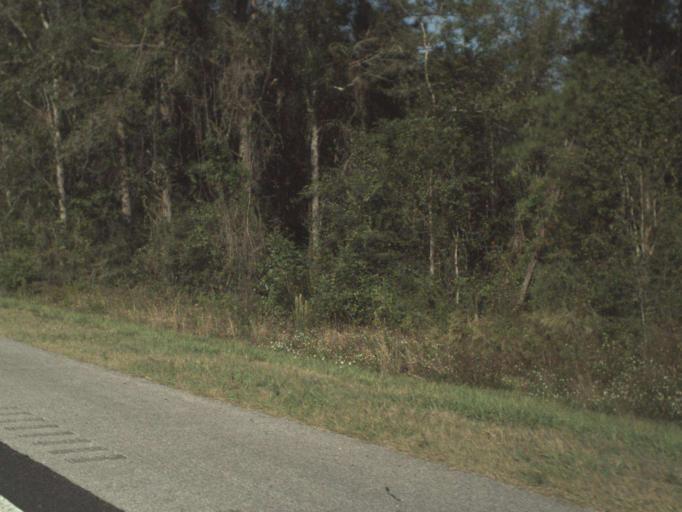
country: US
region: Florida
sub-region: Holmes County
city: Bonifay
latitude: 30.7602
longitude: -85.7998
